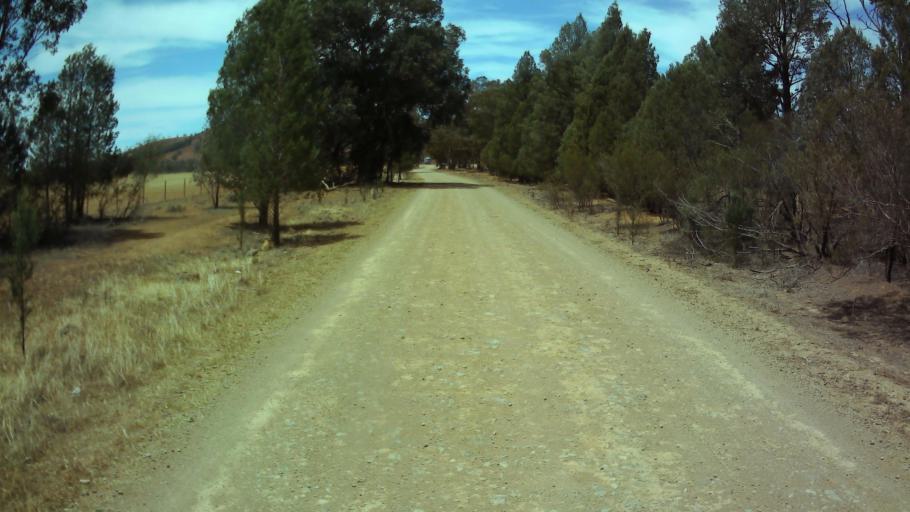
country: AU
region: New South Wales
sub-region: Weddin
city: Grenfell
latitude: -33.7624
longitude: 148.1316
